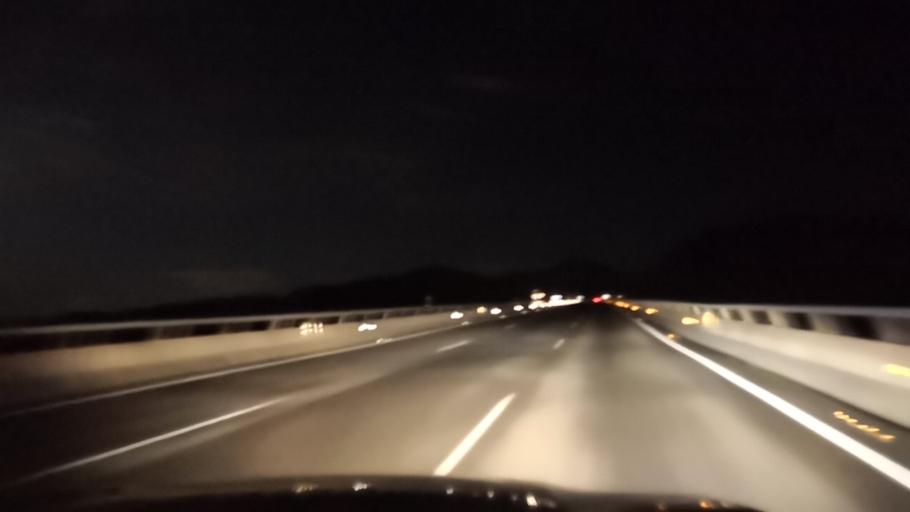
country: ES
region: Galicia
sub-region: Provincia de Ourense
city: Allariz
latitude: 42.1938
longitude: -7.7753
